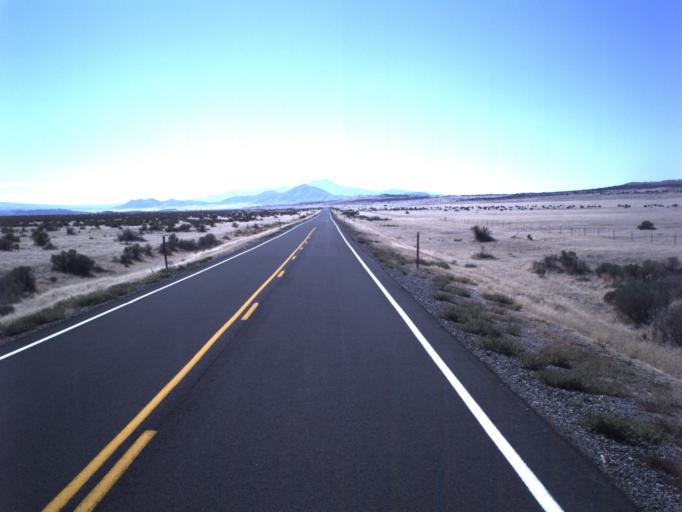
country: US
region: Utah
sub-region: Tooele County
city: Grantsville
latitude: 40.2858
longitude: -112.7421
